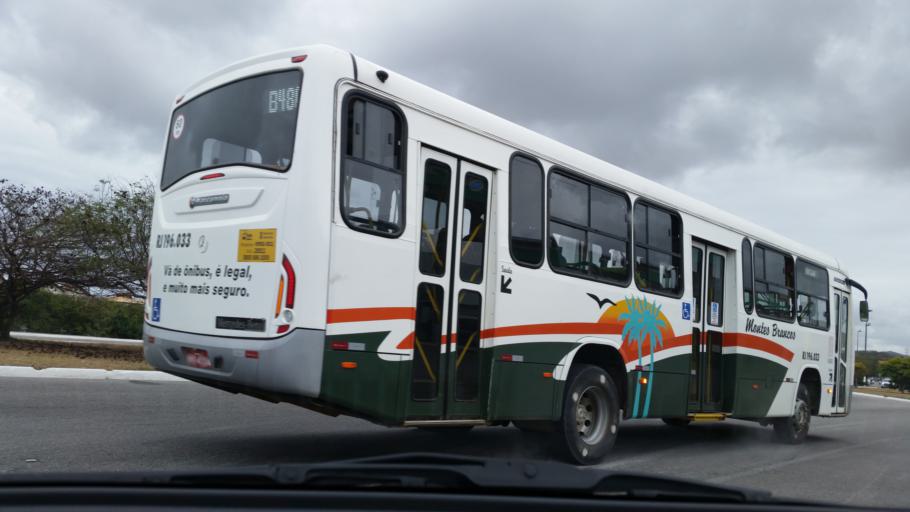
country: BR
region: Rio de Janeiro
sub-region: Cabo Frio
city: Cabo Frio
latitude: -22.8727
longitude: -42.0232
